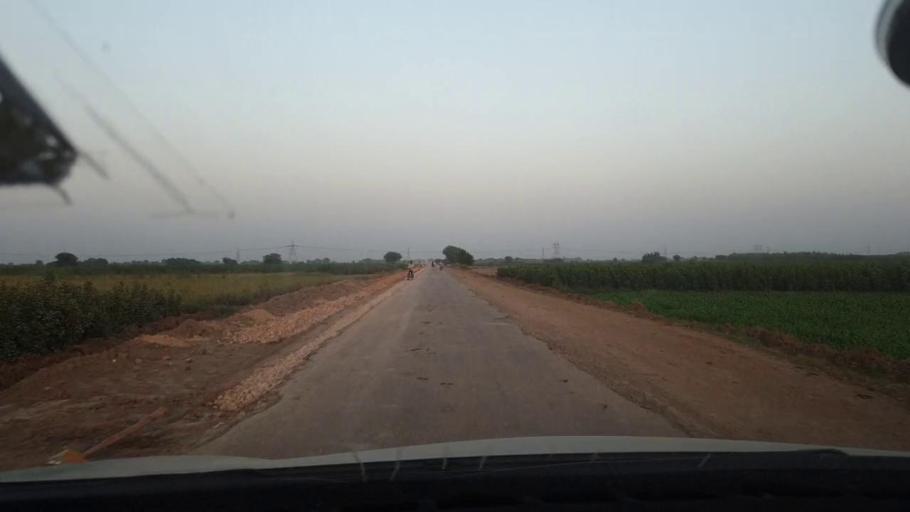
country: PK
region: Sindh
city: Bhit Shah
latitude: 25.7528
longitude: 68.5262
